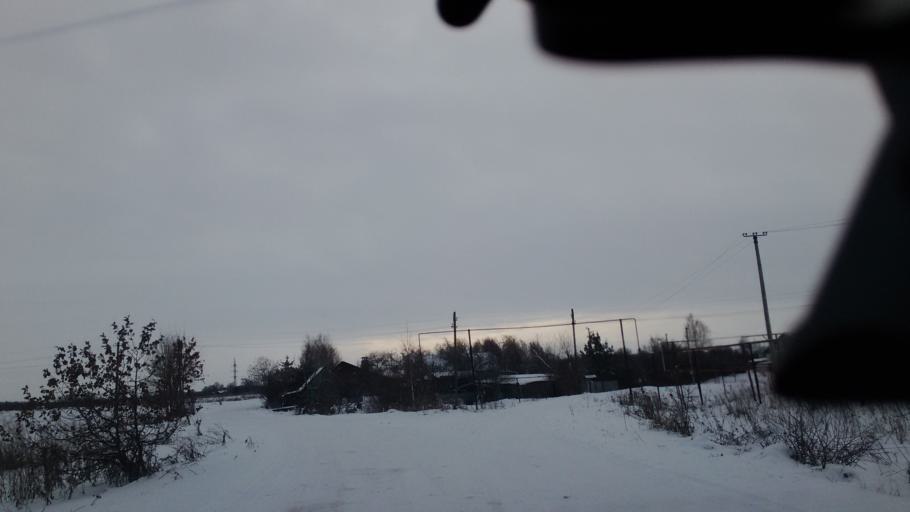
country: RU
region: Tula
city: Bogoroditsk
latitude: 53.7517
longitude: 38.1062
